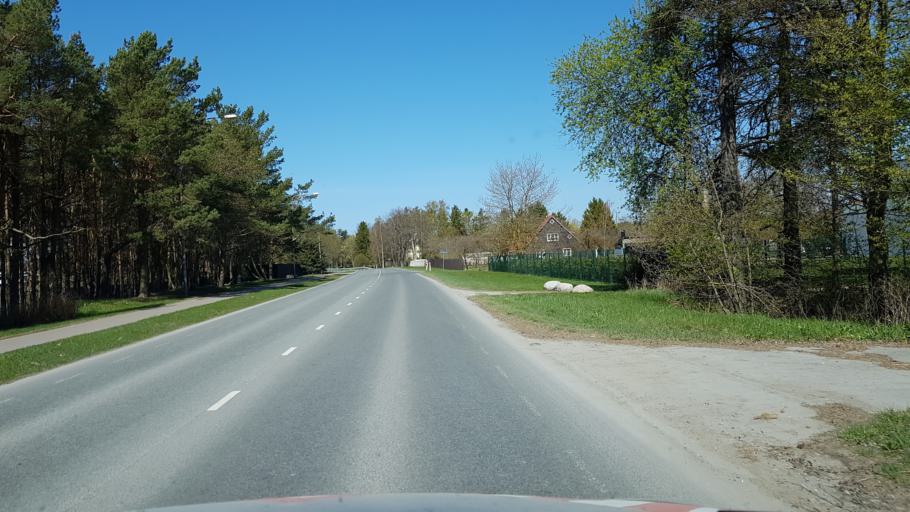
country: EE
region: Harju
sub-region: Viimsi vald
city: Haabneeme
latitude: 59.5185
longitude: 24.8107
